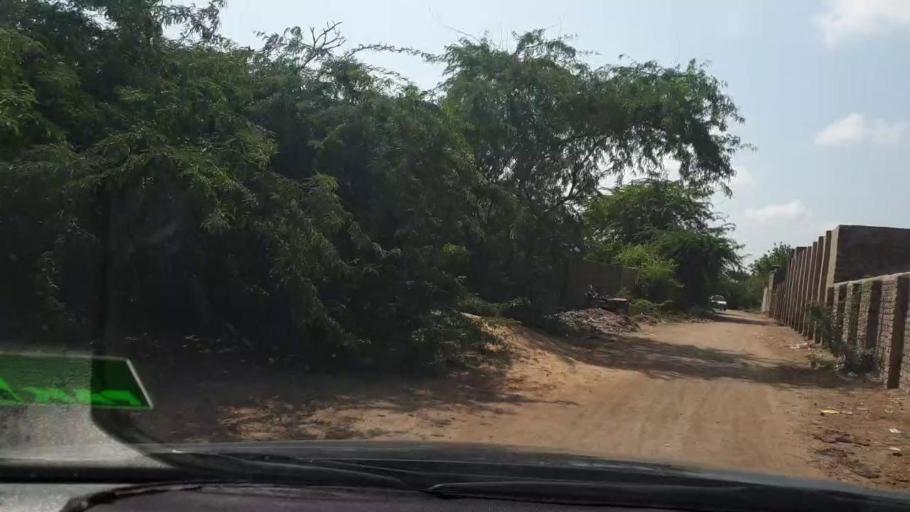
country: PK
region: Sindh
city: Tando Bago
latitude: 24.9263
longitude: 69.0550
